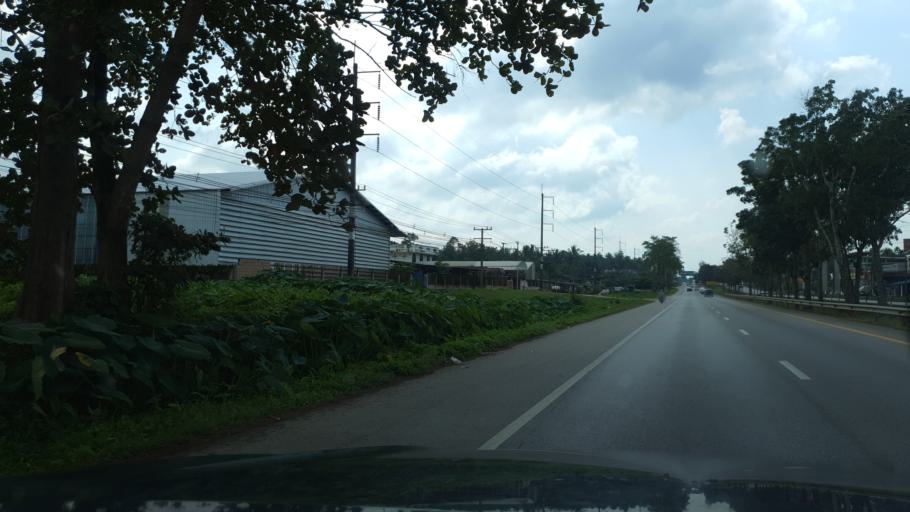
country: TH
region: Chumphon
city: Tha Sae
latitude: 10.6785
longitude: 99.2030
